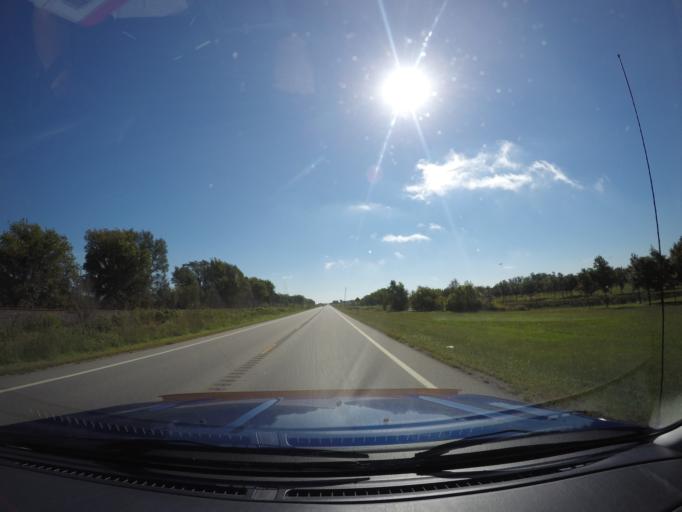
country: US
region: Kansas
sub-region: Shawnee County
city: Rossville
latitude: 39.1183
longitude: -95.9116
